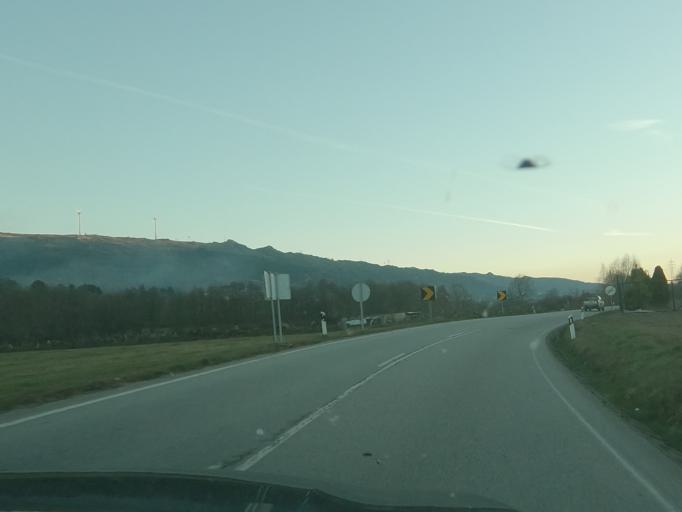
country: PT
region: Vila Real
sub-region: Vila Pouca de Aguiar
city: Vila Pouca de Aguiar
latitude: 41.4595
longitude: -7.6650
